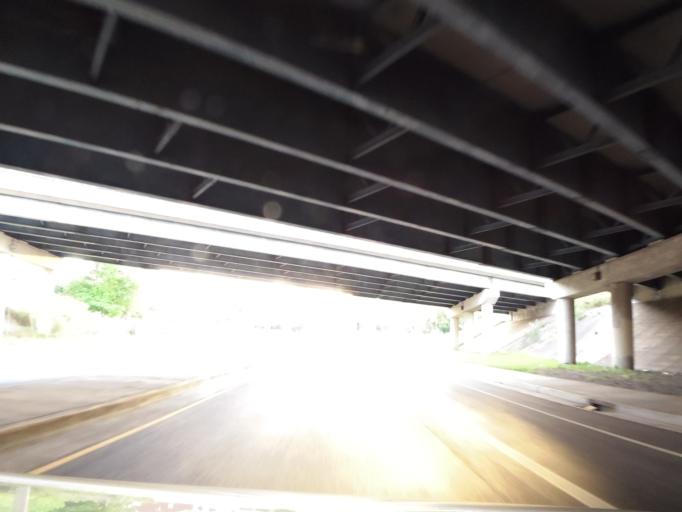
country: US
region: Tennessee
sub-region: Knox County
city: Knoxville
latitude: 35.9713
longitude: -83.9304
